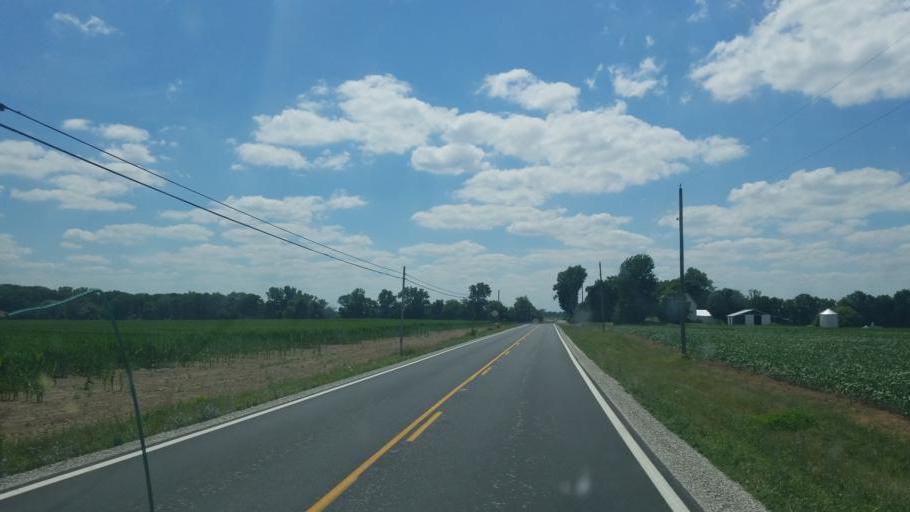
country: US
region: Ohio
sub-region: Defiance County
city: Hicksville
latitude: 41.3191
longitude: -84.7194
